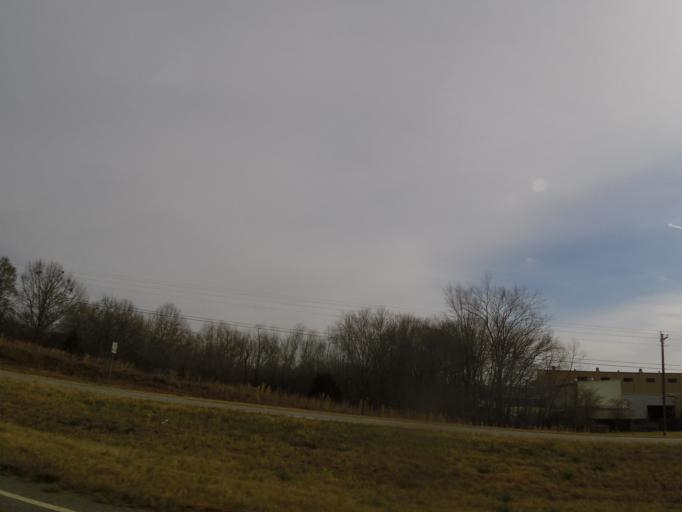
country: US
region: Alabama
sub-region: Montgomery County
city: Pike Road
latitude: 32.2147
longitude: -86.1179
